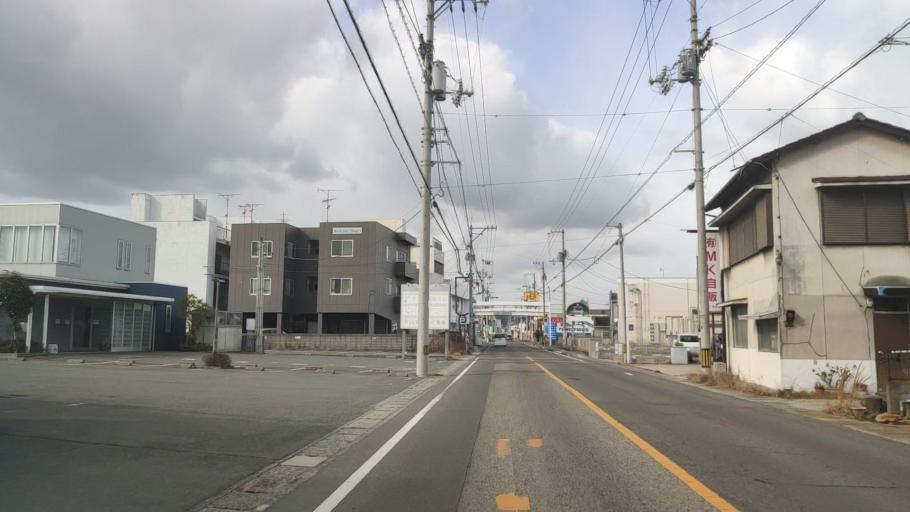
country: JP
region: Ehime
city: Saijo
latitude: 34.0496
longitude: 133.0152
